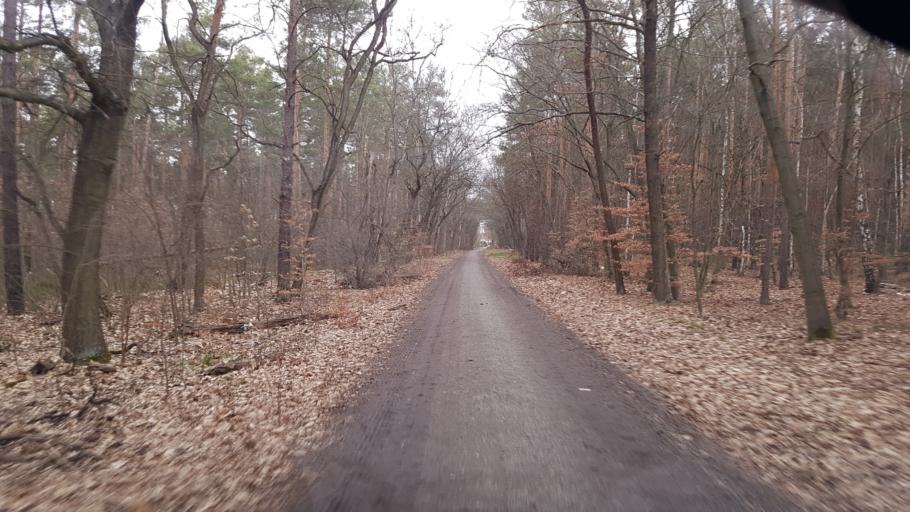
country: DE
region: Brandenburg
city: Finsterwalde
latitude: 51.5792
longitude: 13.6999
